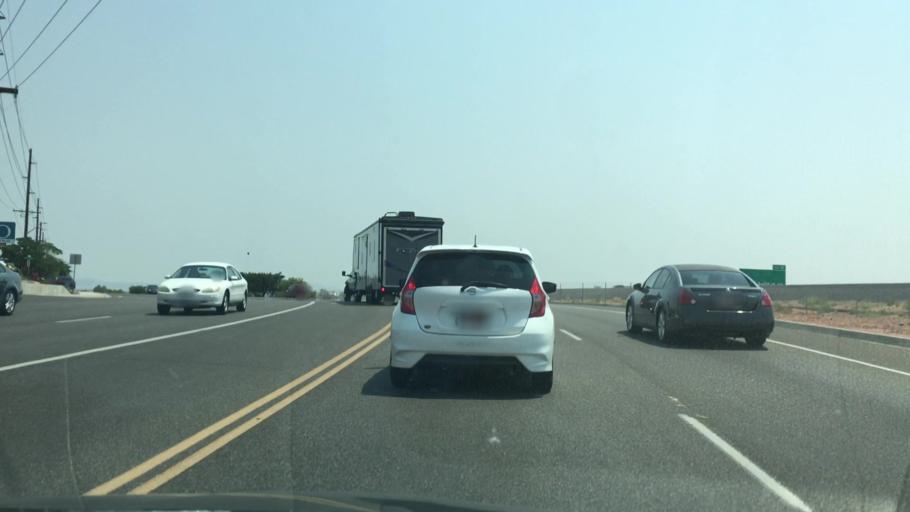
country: US
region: Utah
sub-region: Washington County
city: Washington
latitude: 37.1196
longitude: -113.5470
